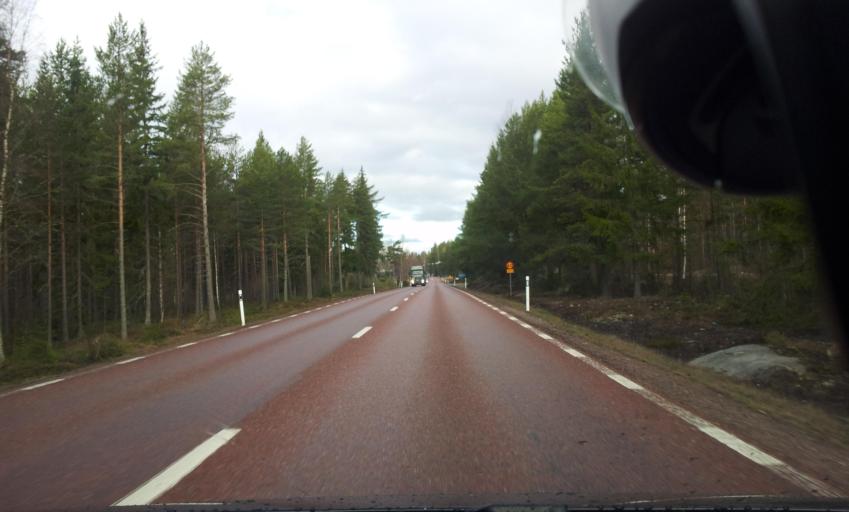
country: SE
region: Gaevleborg
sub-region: Ljusdals Kommun
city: Ljusdal
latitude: 61.8227
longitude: 16.1520
